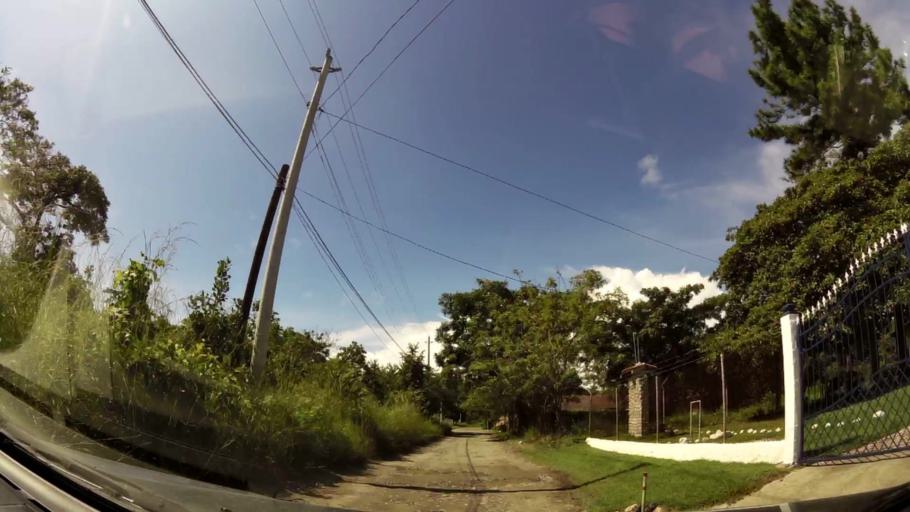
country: PA
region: Panama
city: Nueva Gorgona
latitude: 8.5567
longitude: -79.8690
